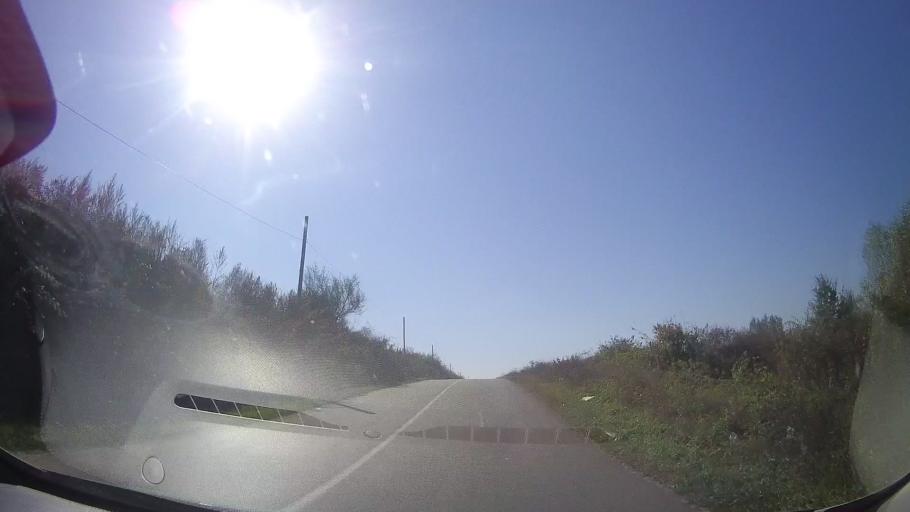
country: RO
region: Timis
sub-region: Comuna Bethausen
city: Bethausen
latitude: 45.8540
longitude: 21.9662
